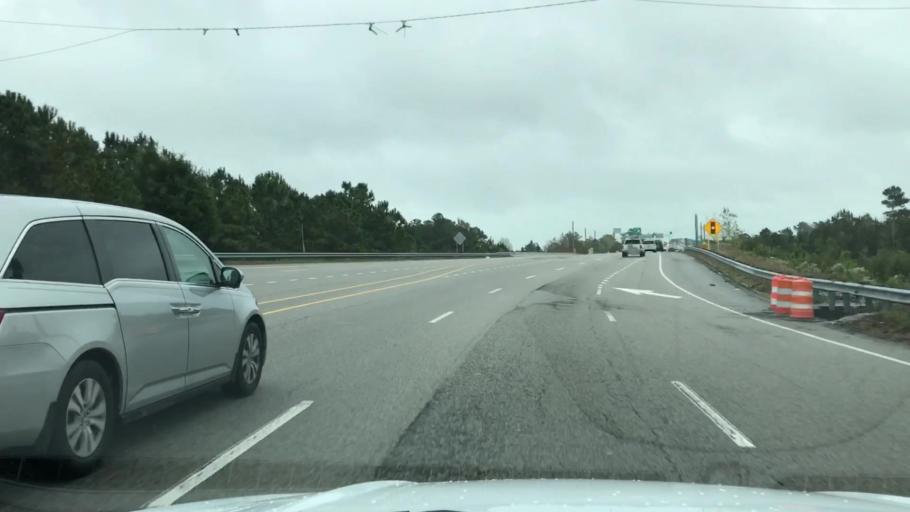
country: US
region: South Carolina
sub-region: Horry County
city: Myrtle Beach
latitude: 33.7552
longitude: -78.8536
